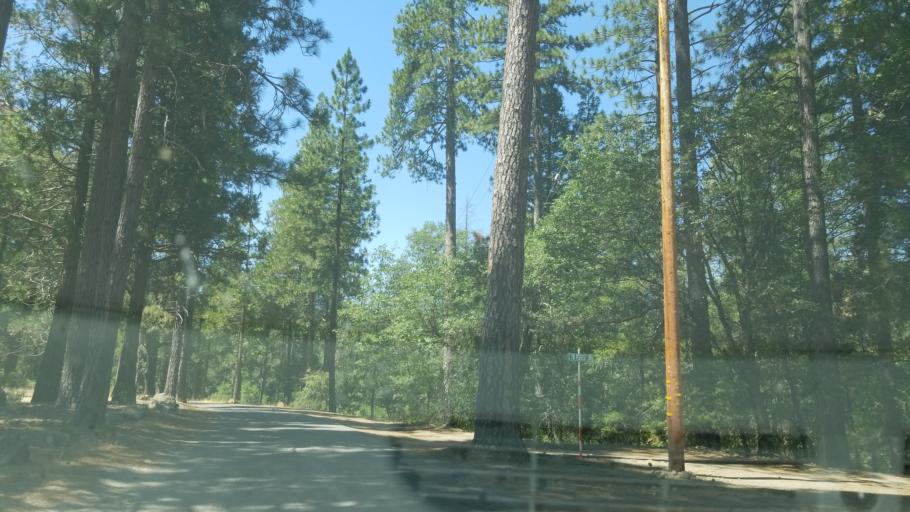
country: US
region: California
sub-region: Madera County
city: Ahwahnee
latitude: 37.5410
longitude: -119.6482
